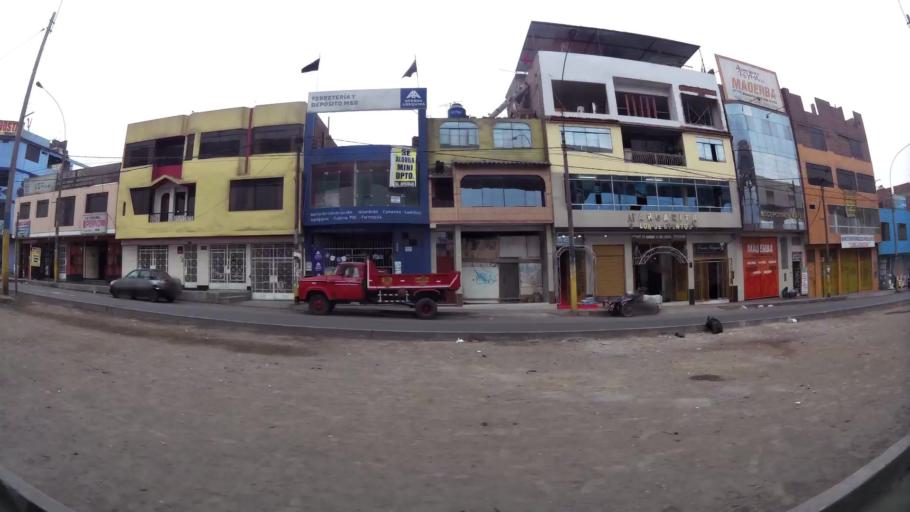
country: PE
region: Lima
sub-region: Lima
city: Independencia
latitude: -11.9619
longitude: -76.9889
